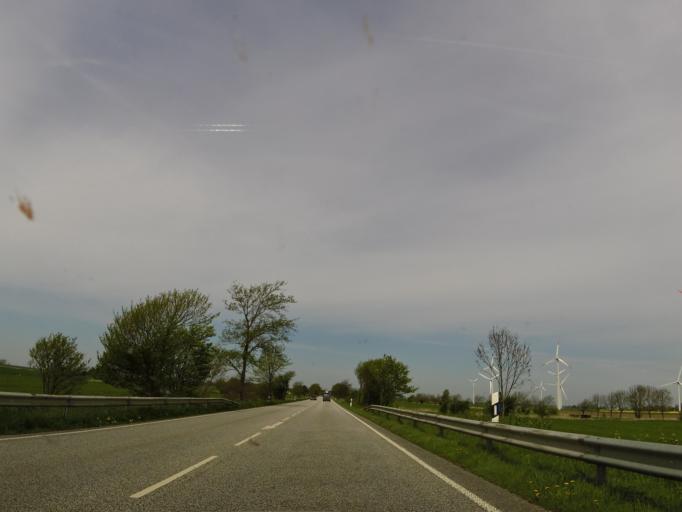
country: DE
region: Schleswig-Holstein
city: Hemme
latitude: 54.2796
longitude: 9.0019
